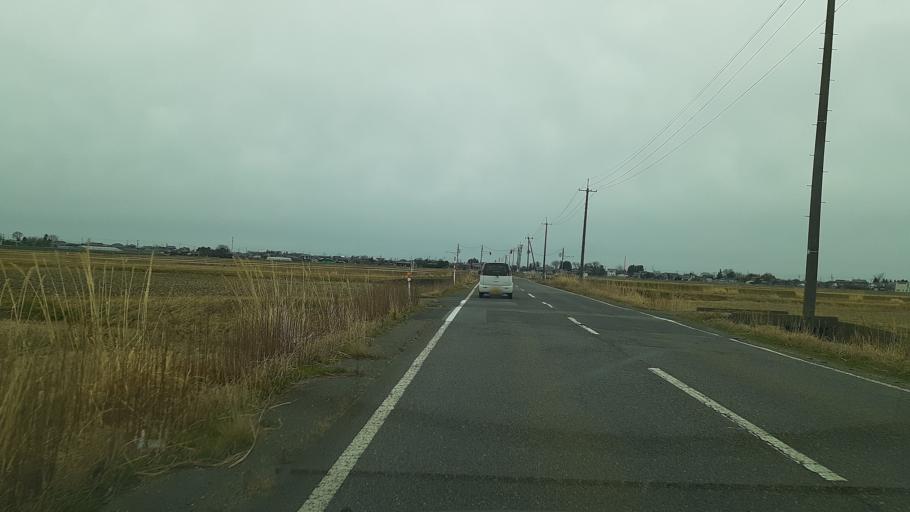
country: JP
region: Niigata
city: Niitsu-honcho
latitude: 37.8288
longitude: 139.0834
